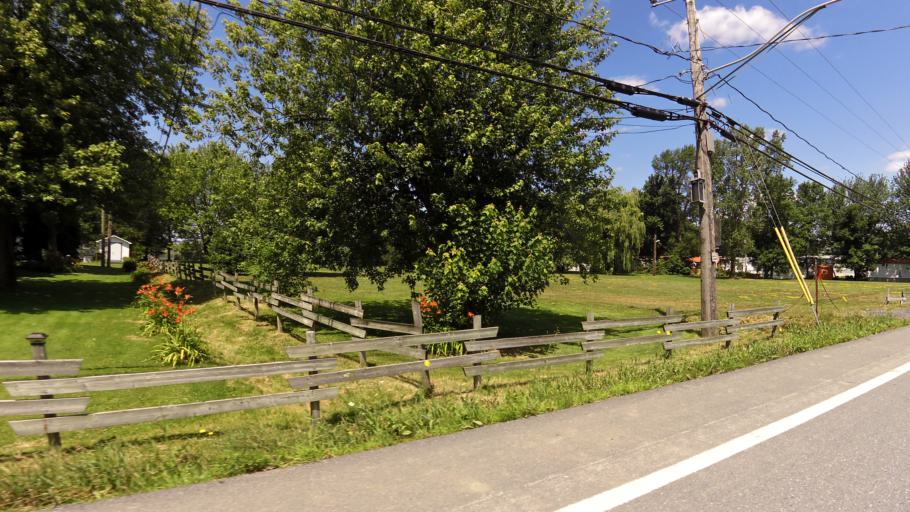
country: CA
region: Quebec
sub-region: Monteregie
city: Saint-Jean-sur-Richelieu
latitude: 45.3456
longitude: -73.2565
